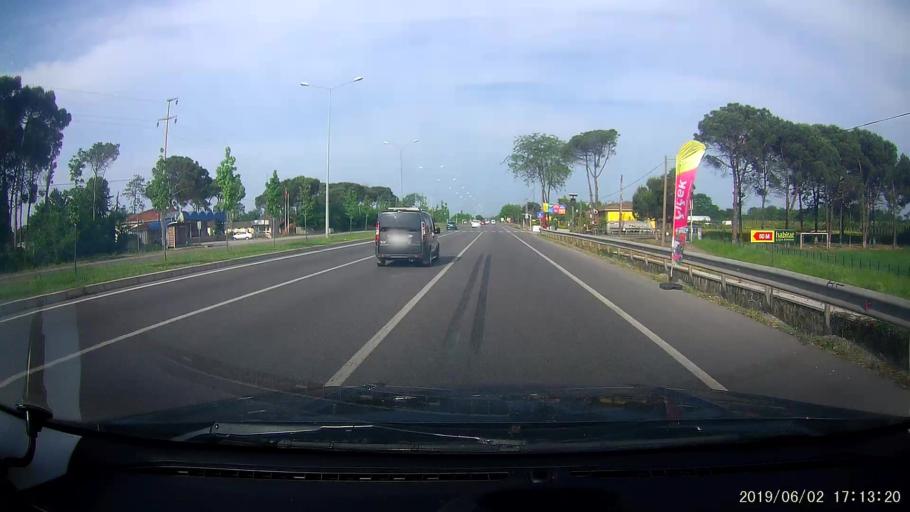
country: TR
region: Samsun
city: Tekkekoy
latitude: 41.2308
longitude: 36.5059
